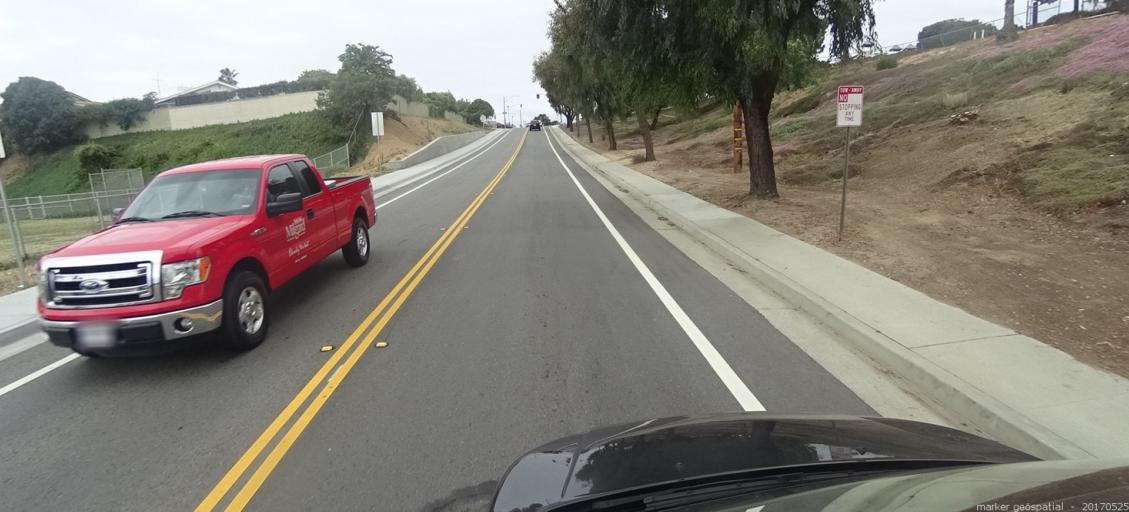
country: US
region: California
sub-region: Los Angeles County
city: Redondo Beach
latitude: 33.8554
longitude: -118.3767
